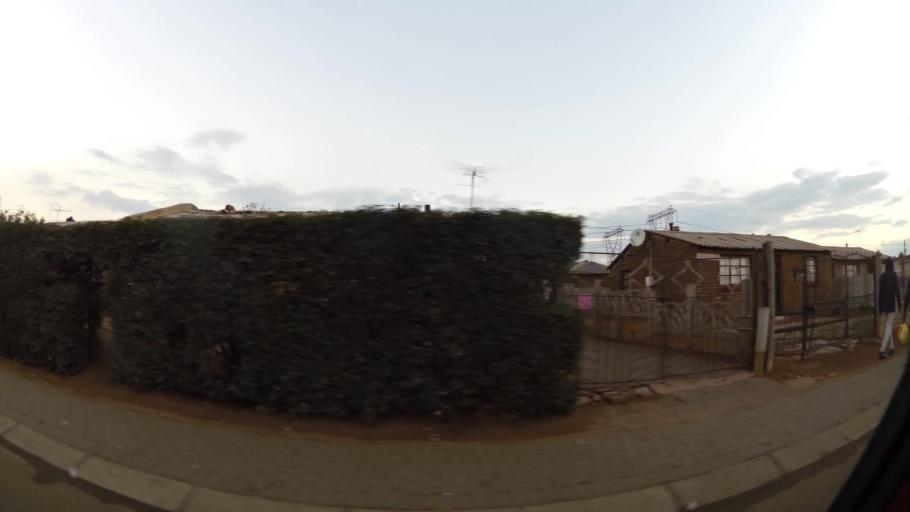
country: ZA
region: Gauteng
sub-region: City of Johannesburg Metropolitan Municipality
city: Orange Farm
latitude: -26.5581
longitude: 27.8656
